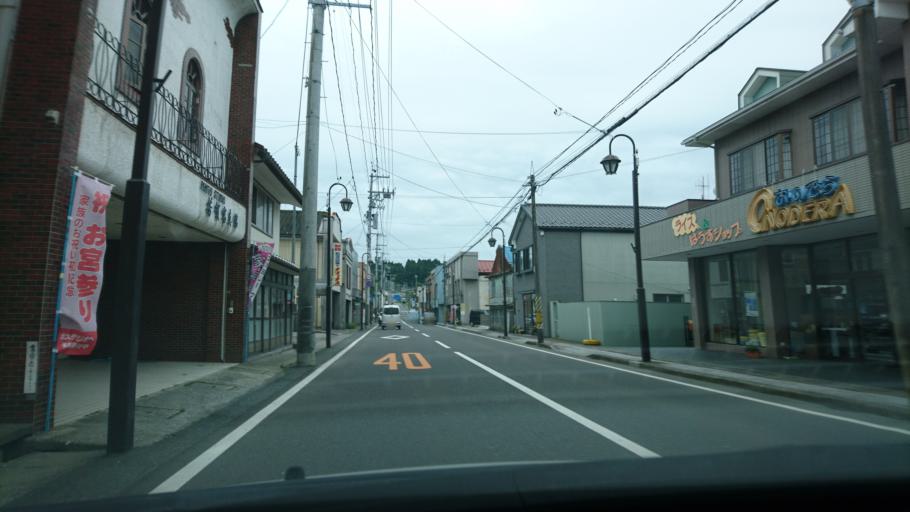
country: JP
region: Iwate
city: Ofunato
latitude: 38.7919
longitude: 141.5048
